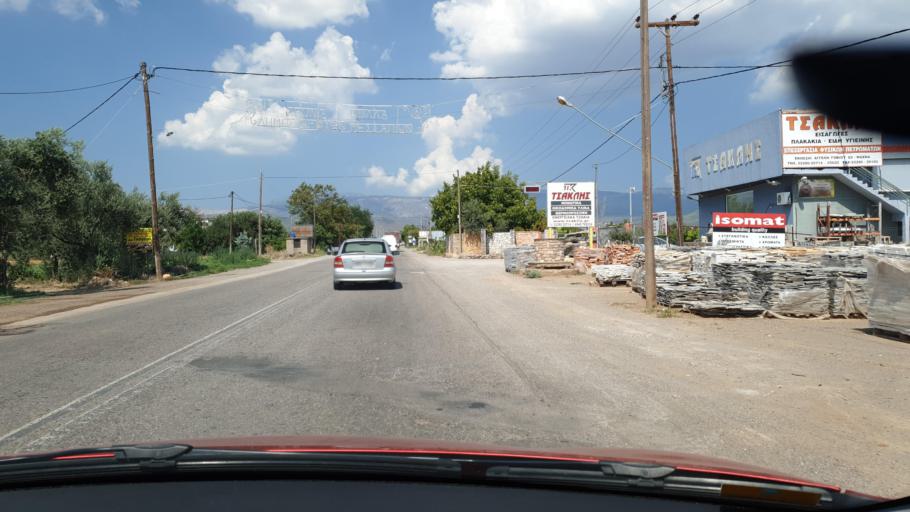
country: GR
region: Central Greece
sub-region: Nomos Evvoias
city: Kastella
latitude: 38.5538
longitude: 23.6318
